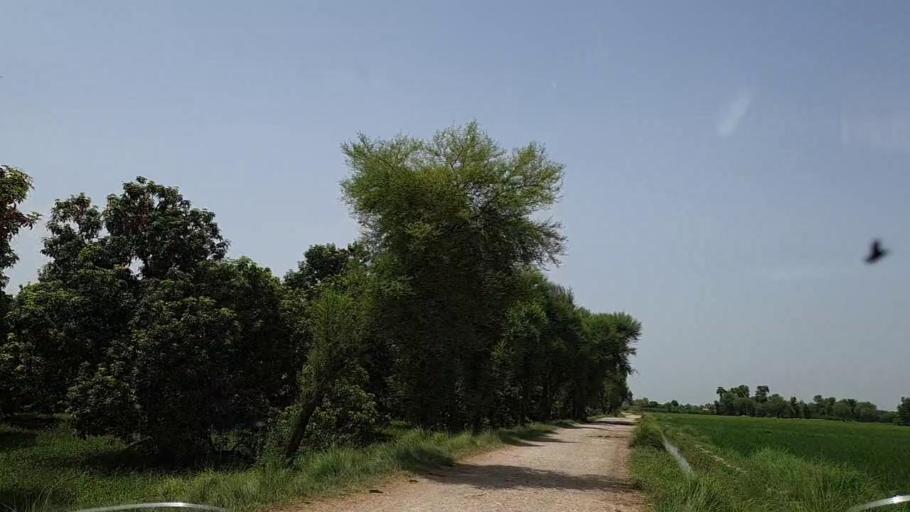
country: PK
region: Sindh
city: Tharu Shah
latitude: 26.9906
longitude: 68.0835
